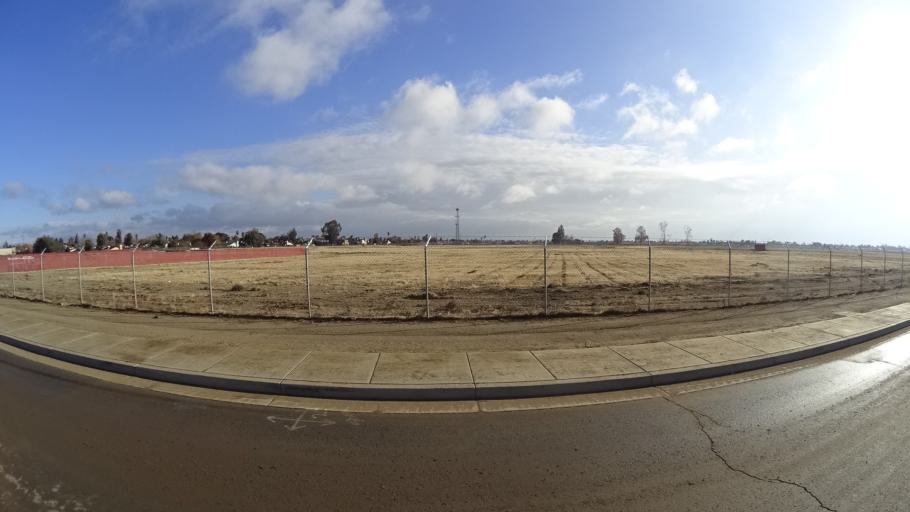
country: US
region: California
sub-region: Kern County
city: Greenfield
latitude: 35.2907
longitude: -119.0270
